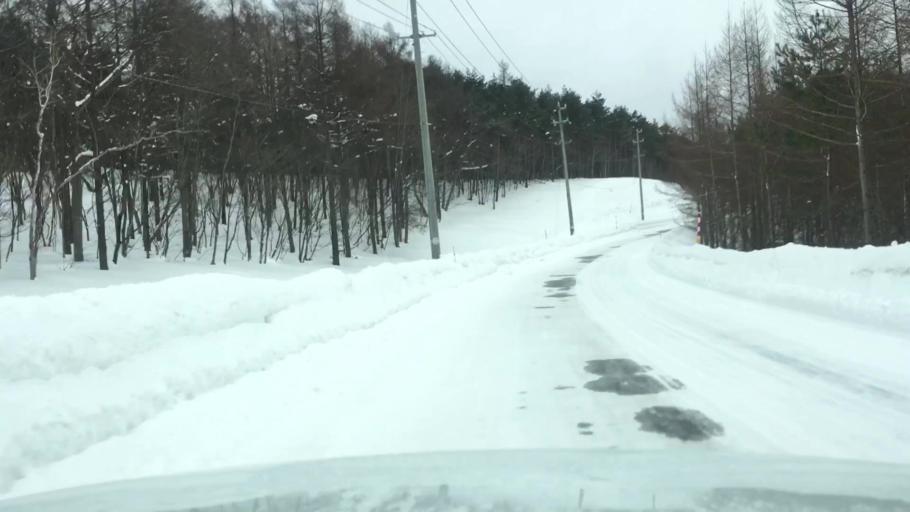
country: JP
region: Iwate
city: Shizukuishi
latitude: 39.9789
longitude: 141.0005
